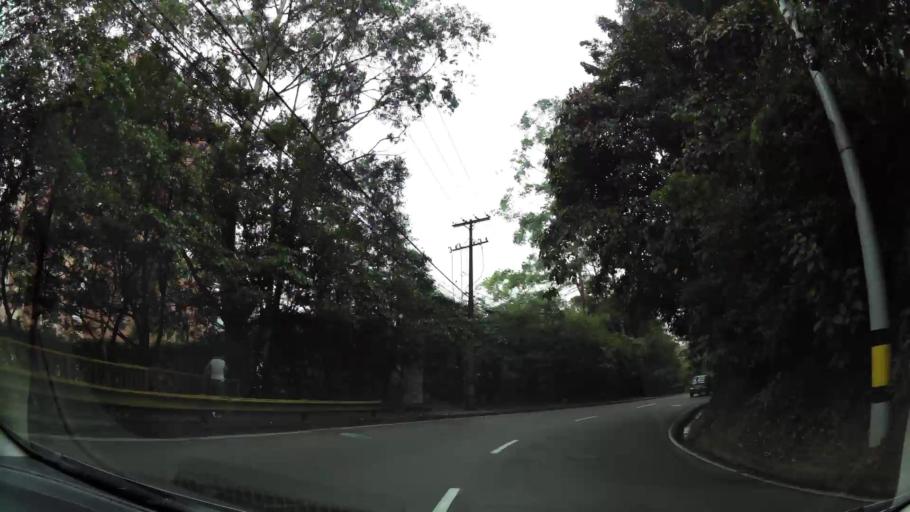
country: CO
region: Antioquia
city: Envigado
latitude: 6.1936
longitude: -75.5599
